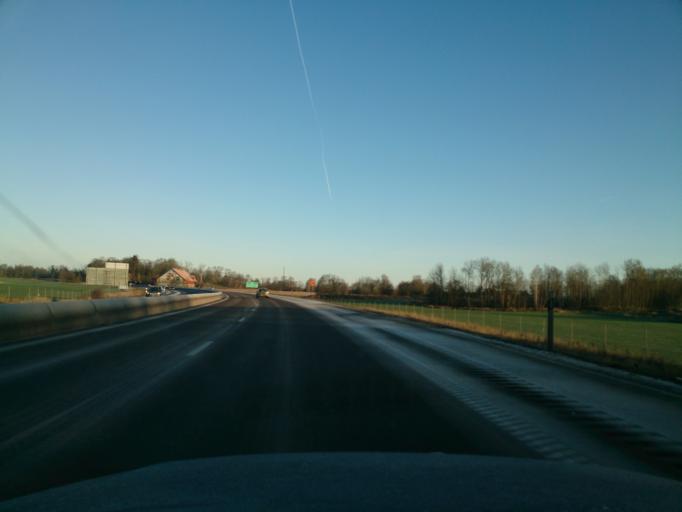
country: SE
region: OEstergoetland
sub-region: Norrkopings Kommun
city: Norrkoping
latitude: 58.5855
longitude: 16.1253
